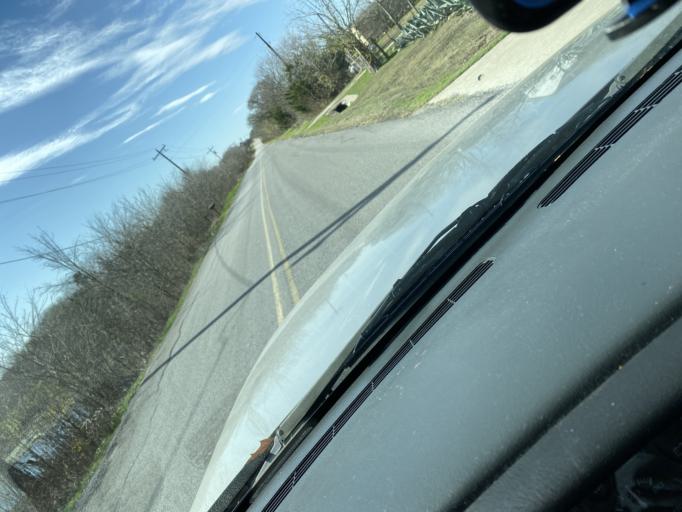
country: US
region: Texas
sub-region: Travis County
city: Onion Creek
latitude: 30.0873
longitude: -97.6992
